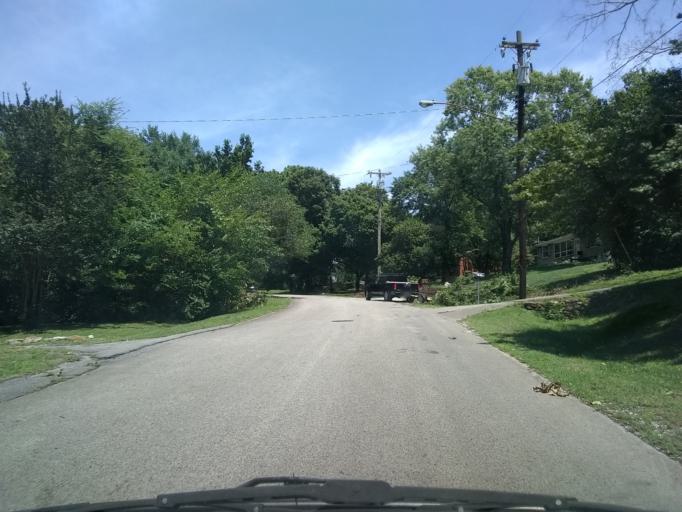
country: US
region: Tennessee
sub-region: Davidson County
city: Nashville
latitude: 36.1353
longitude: -86.7082
